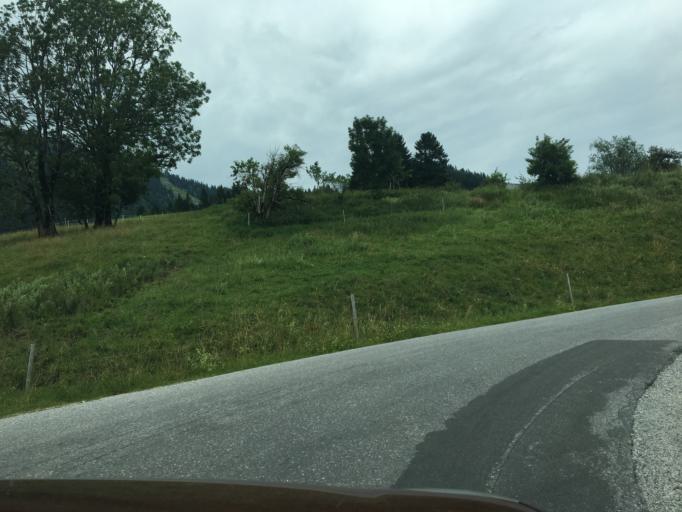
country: AT
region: Salzburg
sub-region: Politischer Bezirk Hallein
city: Abtenau
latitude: 47.6049
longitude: 13.3688
